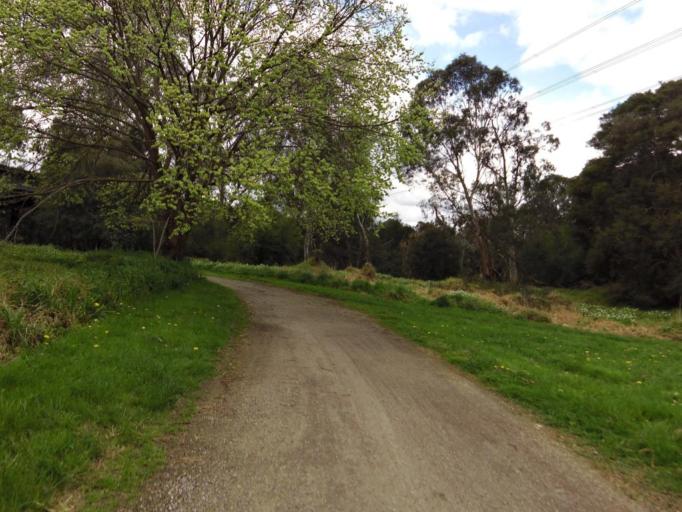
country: AU
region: Victoria
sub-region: Manningham
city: Bulleen
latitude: -37.7607
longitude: 145.0766
